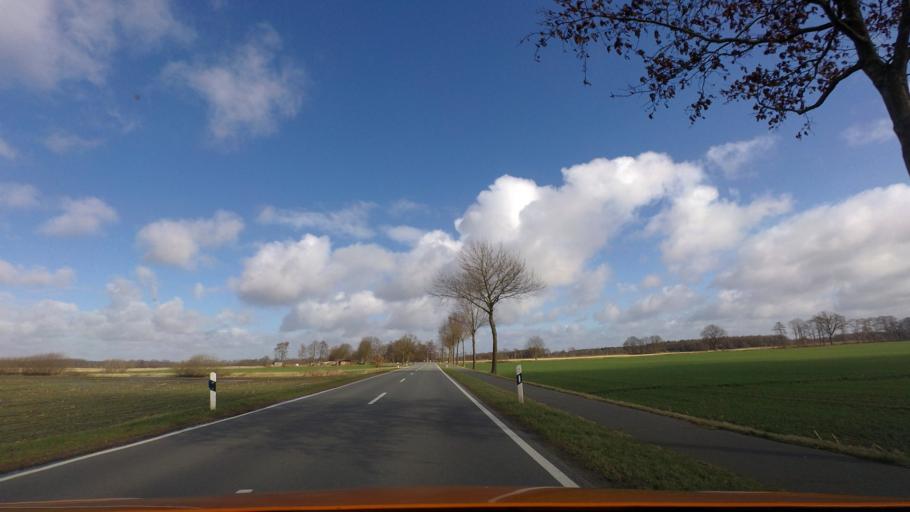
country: DE
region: Lower Saxony
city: Friesoythe
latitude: 53.0567
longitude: 7.9130
